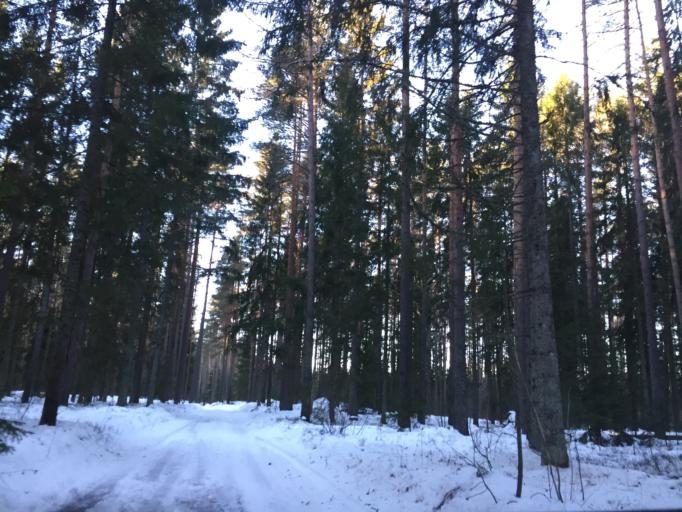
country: LV
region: Kegums
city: Kegums
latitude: 56.7343
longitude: 24.6518
